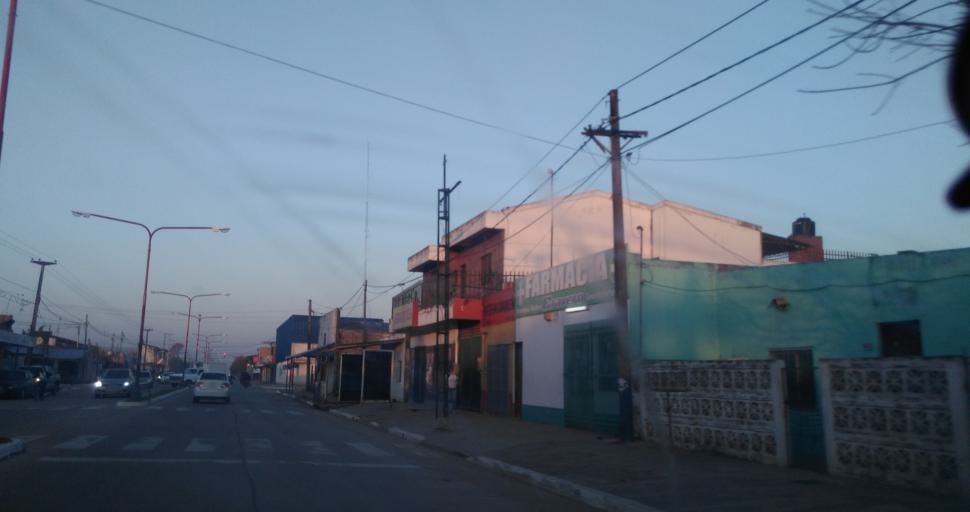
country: AR
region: Chaco
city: Resistencia
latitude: -27.4817
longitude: -58.9778
